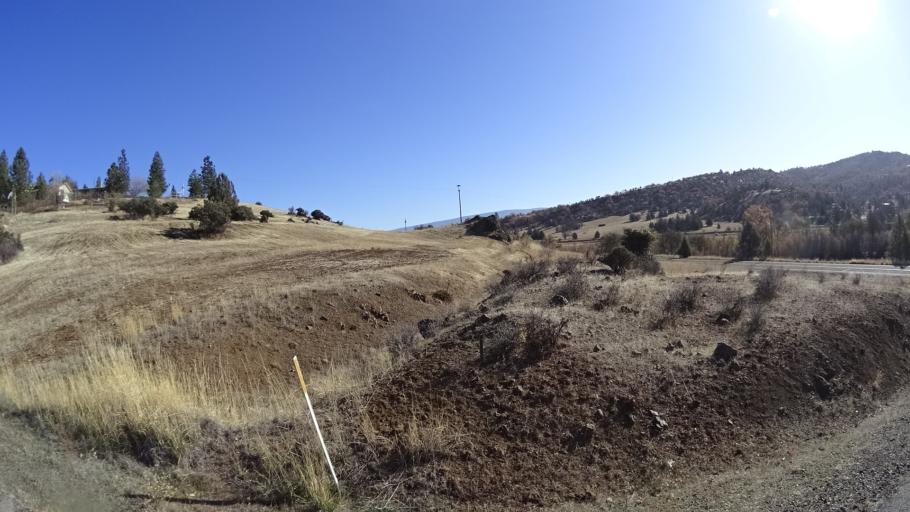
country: US
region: California
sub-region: Siskiyou County
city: Montague
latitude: 41.8979
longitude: -122.5223
